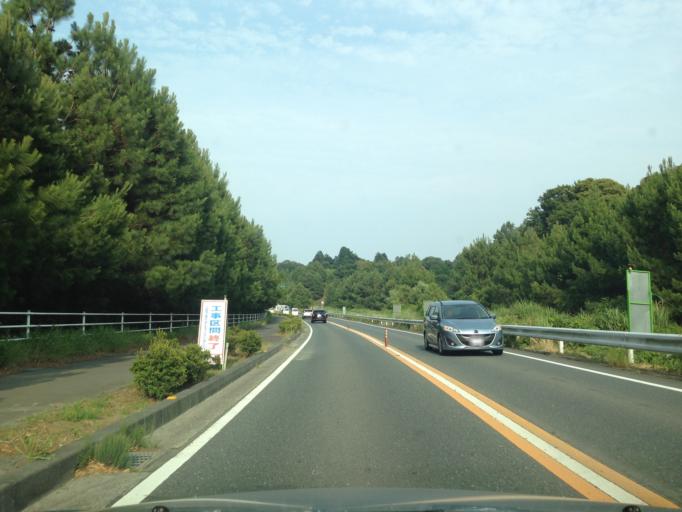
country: JP
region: Shizuoka
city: Kakegawa
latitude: 34.7525
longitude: 138.0058
